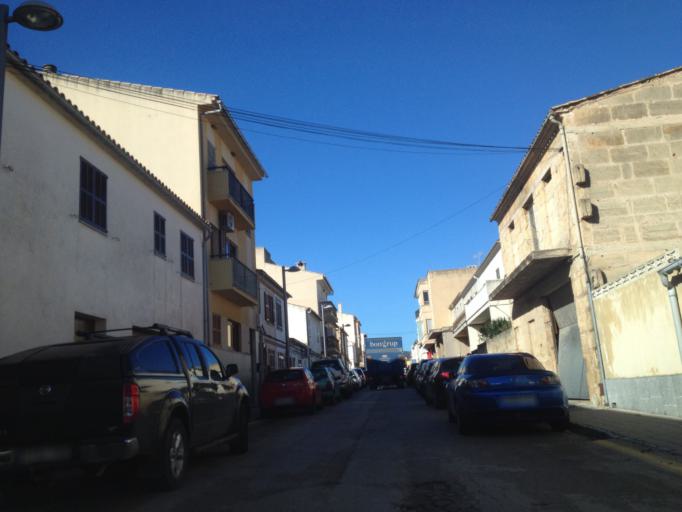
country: ES
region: Balearic Islands
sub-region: Illes Balears
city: Arta
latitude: 39.6915
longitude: 3.3472
